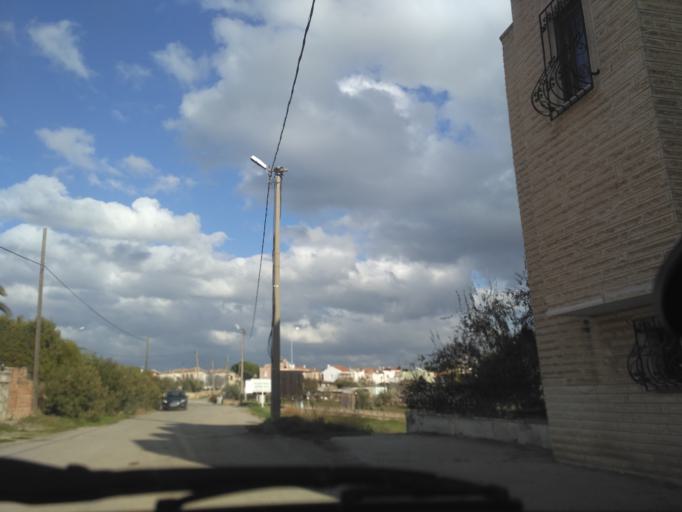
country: TR
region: Balikesir
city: Ayvalik
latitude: 39.3355
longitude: 26.6550
